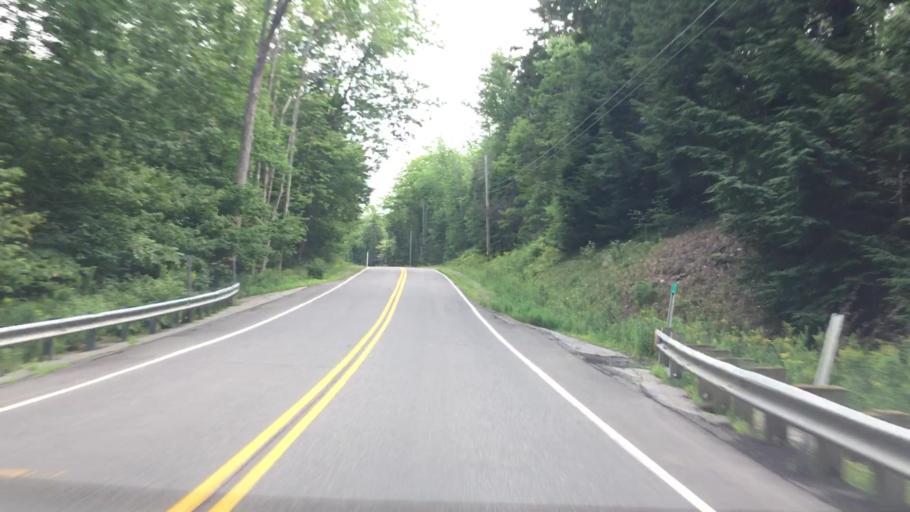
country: US
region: Maine
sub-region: Waldo County
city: Lincolnville
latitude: 44.3447
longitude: -69.0564
